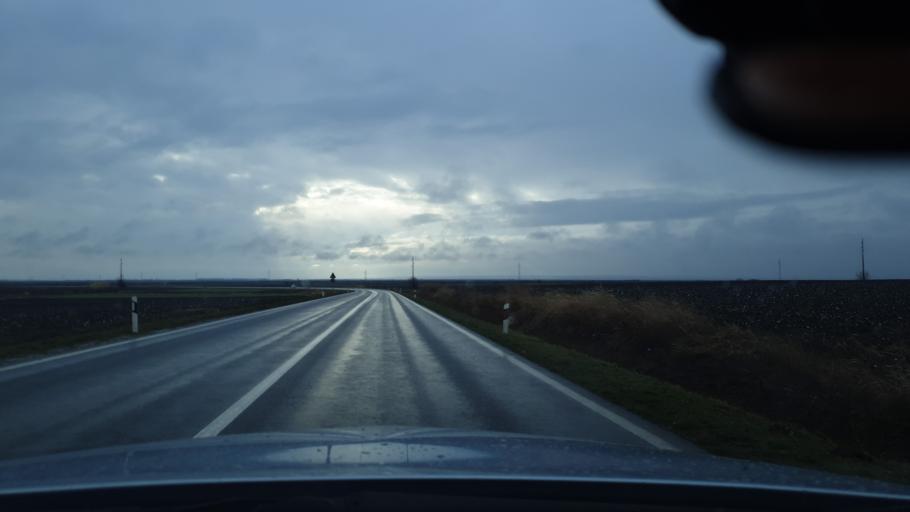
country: RS
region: Autonomna Pokrajina Vojvodina
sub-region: Juznobanatski Okrug
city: Kovin
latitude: 44.8139
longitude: 20.8564
